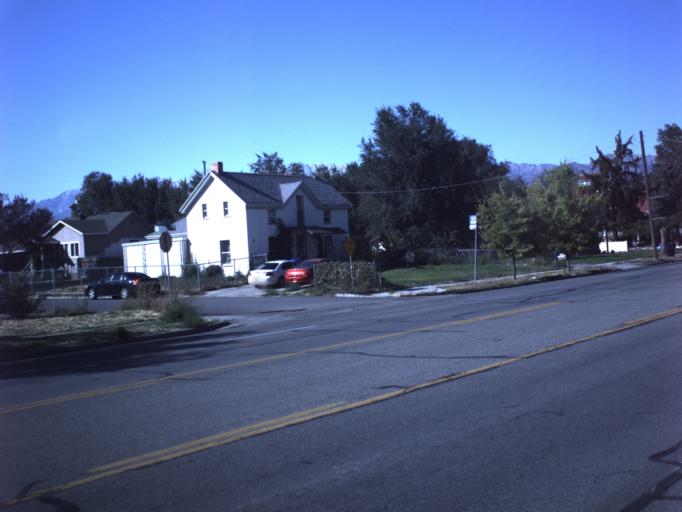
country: US
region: Utah
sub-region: Tooele County
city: Grantsville
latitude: 40.5999
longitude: -112.4603
